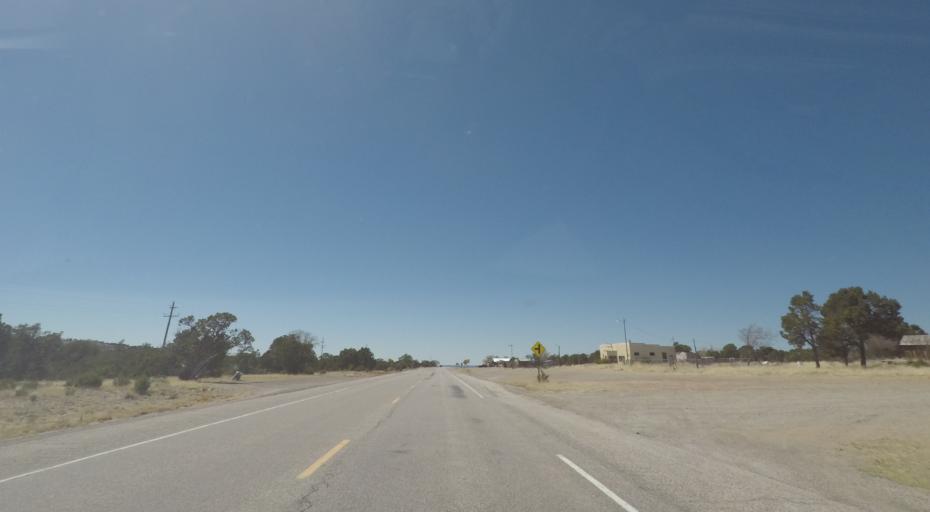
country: US
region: New Mexico
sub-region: Socorro County
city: Alamo
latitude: 34.2978
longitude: -108.1272
